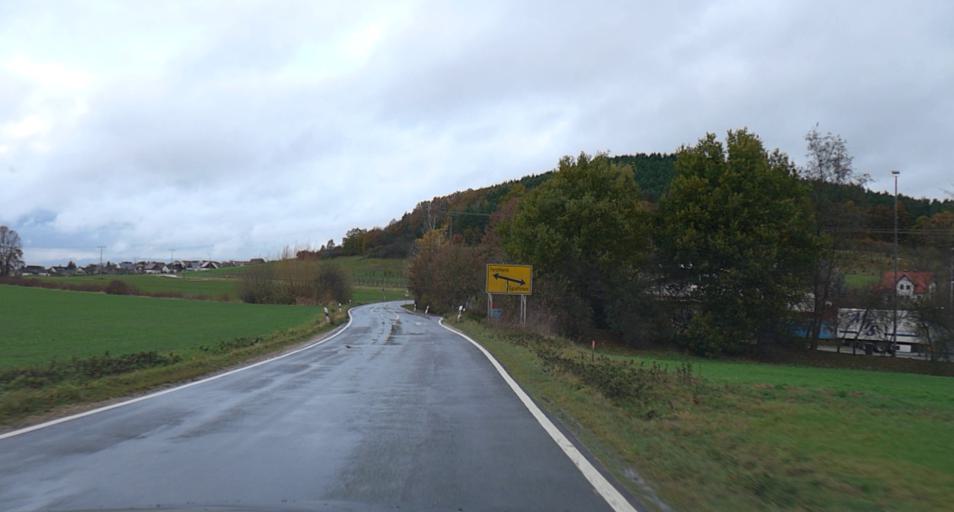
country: DE
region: Bavaria
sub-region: Upper Franconia
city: Leutenbach
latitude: 49.6995
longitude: 11.1609
